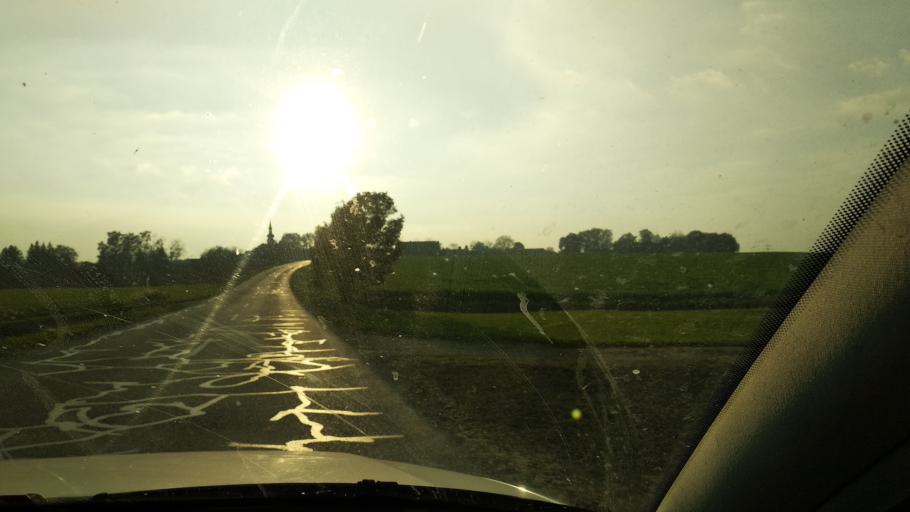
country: DE
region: Bavaria
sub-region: Upper Bavaria
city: Pastetten
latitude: 48.2144
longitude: 11.9421
